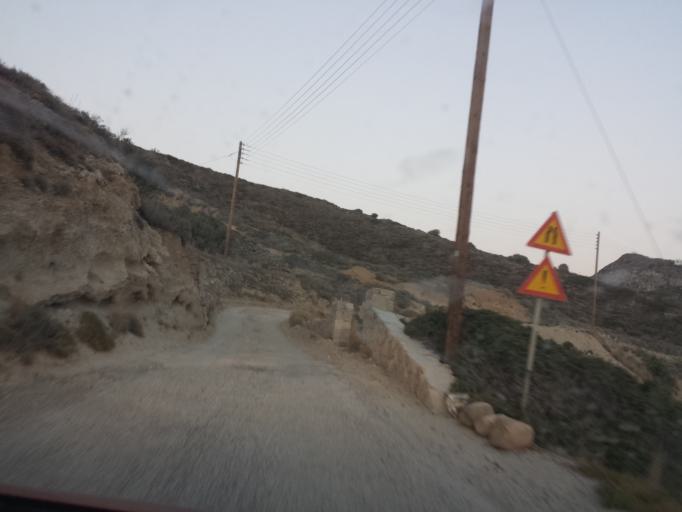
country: GR
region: South Aegean
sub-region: Nomos Kykladon
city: Milos
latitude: 36.7532
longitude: 24.4149
